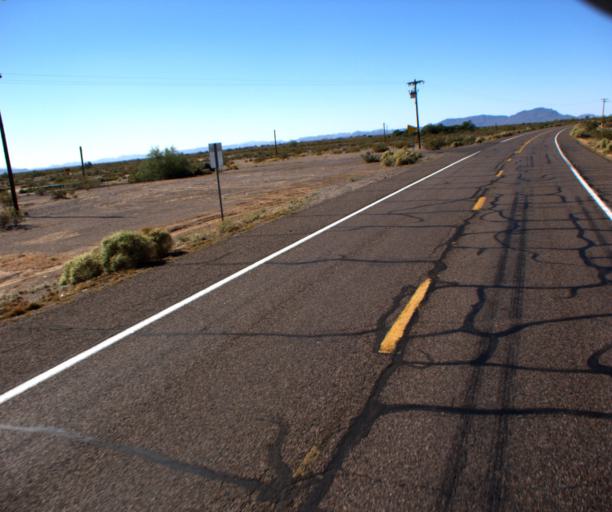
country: US
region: Arizona
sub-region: Maricopa County
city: Gila Bend
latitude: 32.9159
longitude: -112.7354
